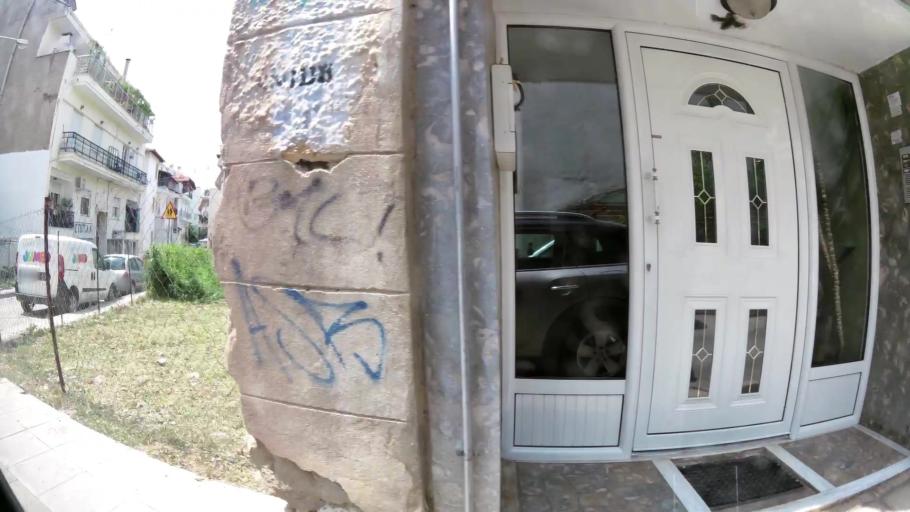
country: GR
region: West Macedonia
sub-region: Nomos Kozanis
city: Kozani
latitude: 40.3037
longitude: 21.7912
